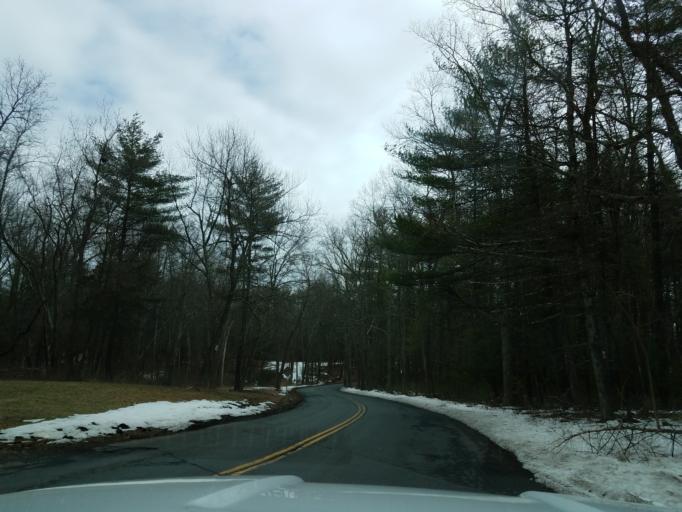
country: US
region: Connecticut
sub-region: Hartford County
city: Farmington
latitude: 41.7779
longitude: -72.8440
